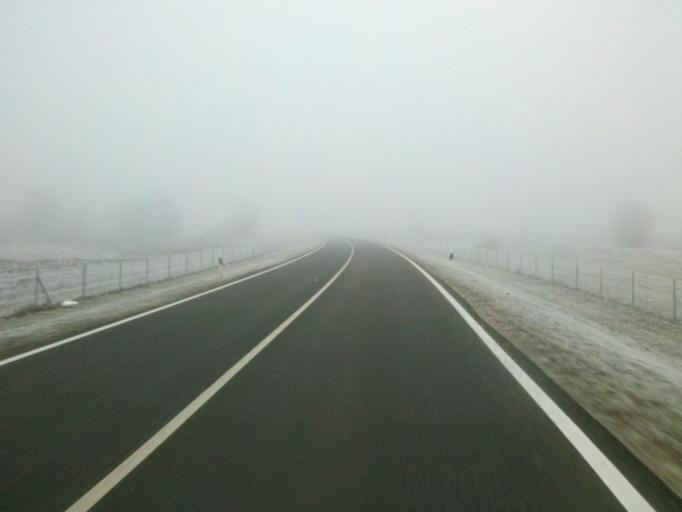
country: HR
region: Varazdinska
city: Jalkovec
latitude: 46.2697
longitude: 16.3365
